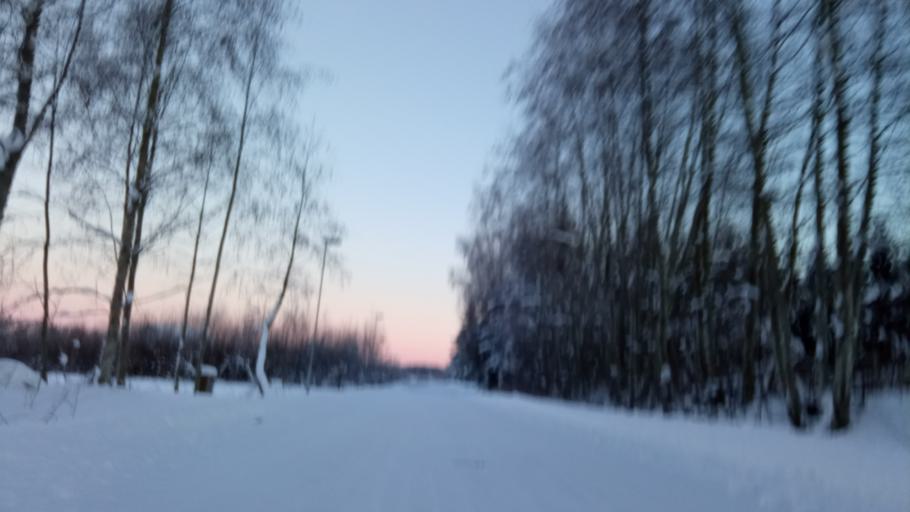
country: FI
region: Southern Ostrobothnia
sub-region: Jaerviseutu
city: Alajaervi
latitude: 62.9905
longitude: 23.8546
